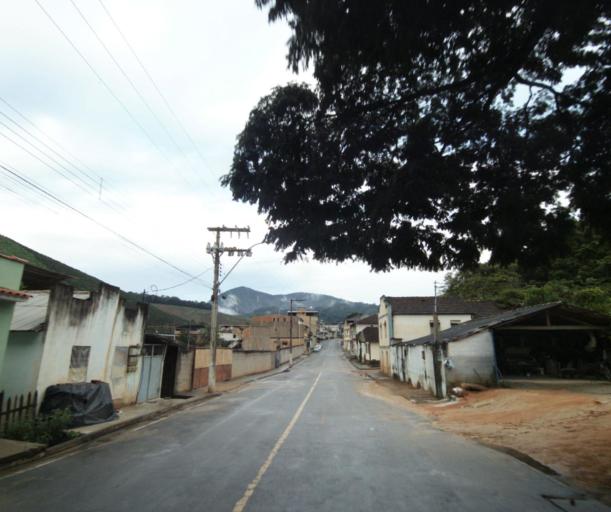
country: BR
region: Espirito Santo
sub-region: Muniz Freire
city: Muniz Freire
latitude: -20.4630
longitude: -41.4213
